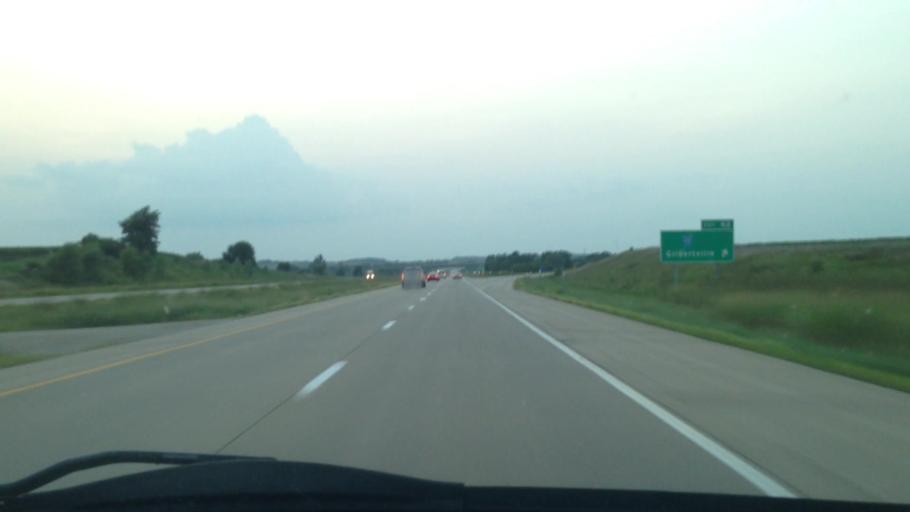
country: US
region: Iowa
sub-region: Black Hawk County
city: La Porte City
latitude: 42.4088
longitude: -92.1652
